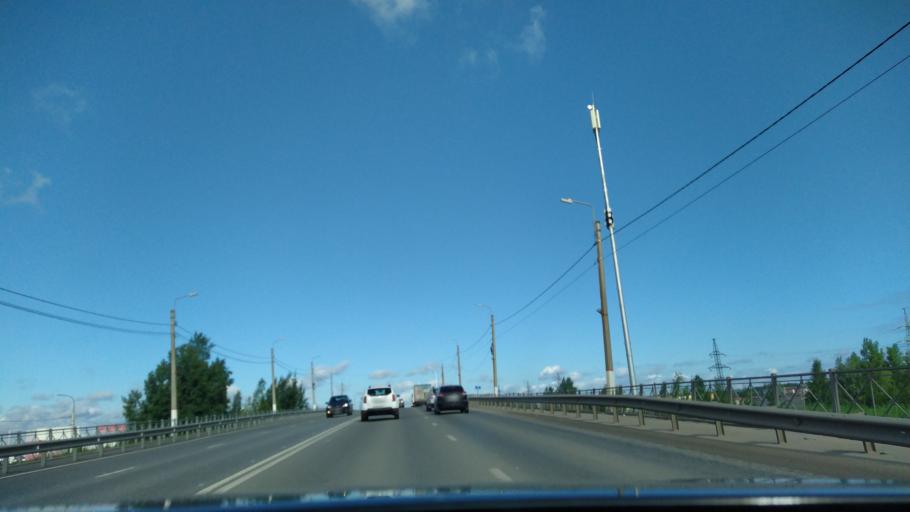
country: RU
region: Leningrad
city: Tosno
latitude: 59.5496
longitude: 30.8611
